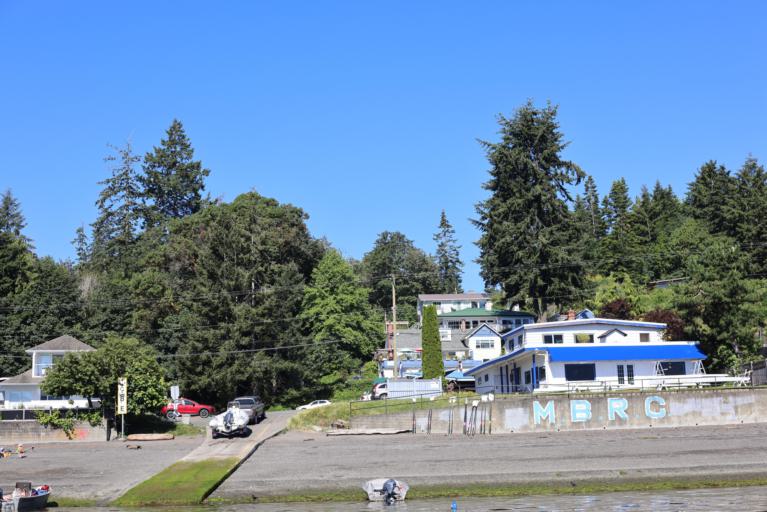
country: CA
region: British Columbia
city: North Cowichan
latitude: 48.8156
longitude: -123.6087
